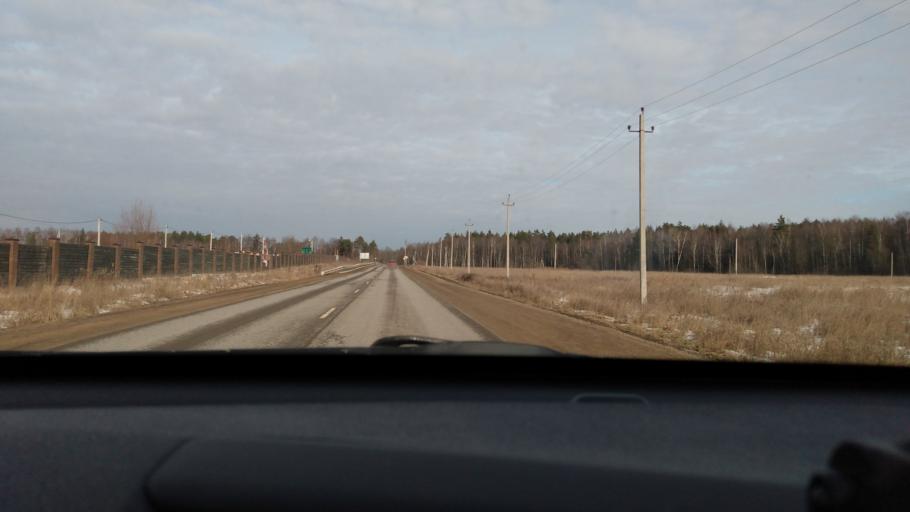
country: RU
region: Moskovskaya
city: Nakhabino
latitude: 55.8758
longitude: 37.1868
